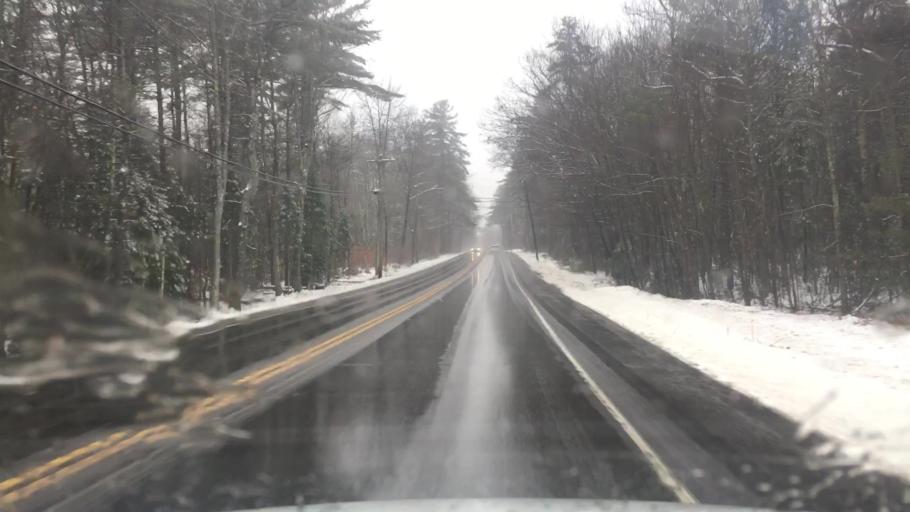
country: US
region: Maine
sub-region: York County
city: Buxton
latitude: 43.7147
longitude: -70.5191
